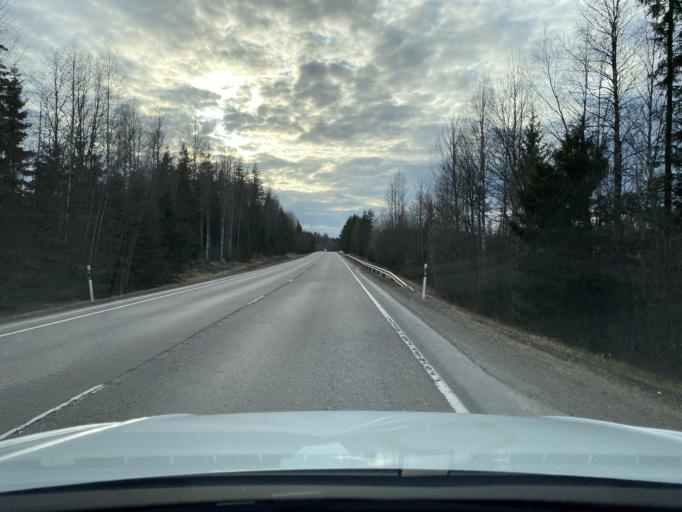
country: FI
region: Haeme
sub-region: Haemeenlinna
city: Renko
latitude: 60.7747
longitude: 24.1957
